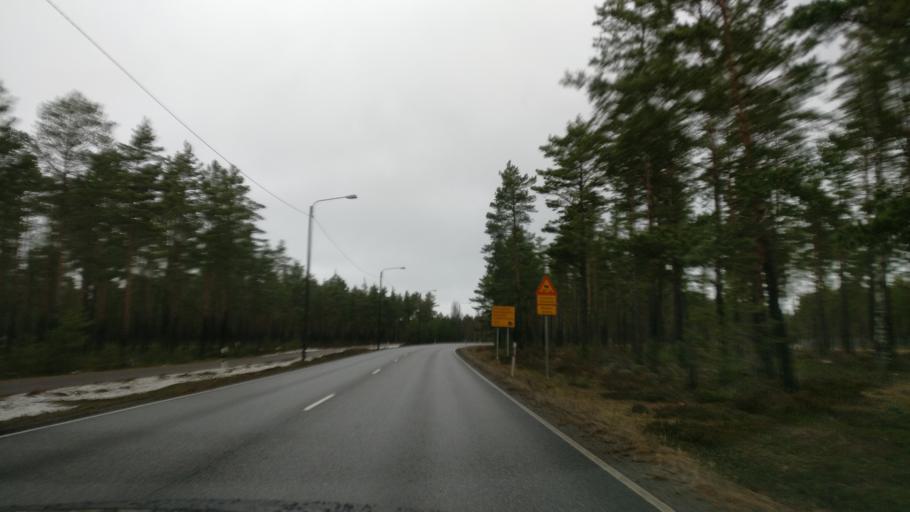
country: FI
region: Uusimaa
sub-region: Raaseporin
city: Hanko
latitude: 59.8473
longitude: 23.0059
